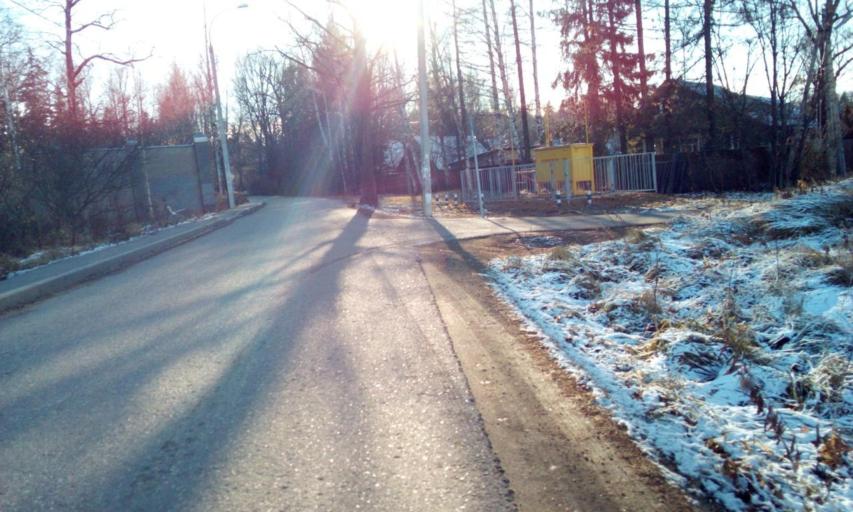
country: RU
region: Moskovskaya
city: Aprelevka
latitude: 55.5436
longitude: 37.0520
